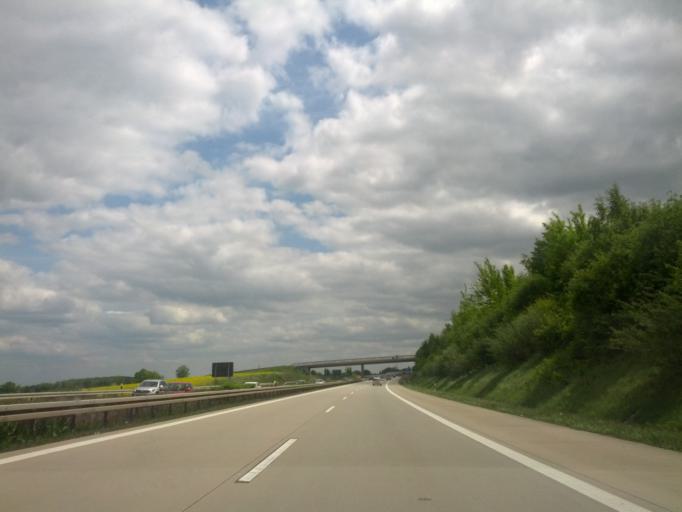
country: DE
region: Saxony
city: Kreischa
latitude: 50.9843
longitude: 13.7844
